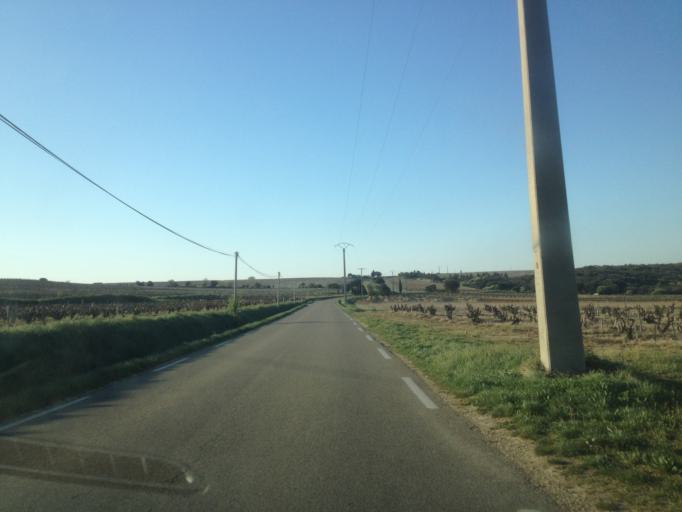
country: FR
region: Provence-Alpes-Cote d'Azur
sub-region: Departement du Vaucluse
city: Chateauneuf-du-Pape
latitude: 44.0783
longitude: 4.8321
